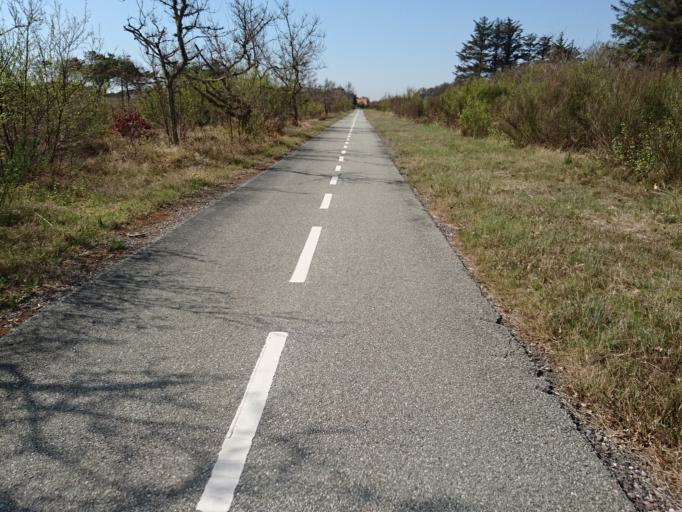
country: DK
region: North Denmark
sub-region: Frederikshavn Kommune
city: Strandby
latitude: 57.6290
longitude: 10.4477
